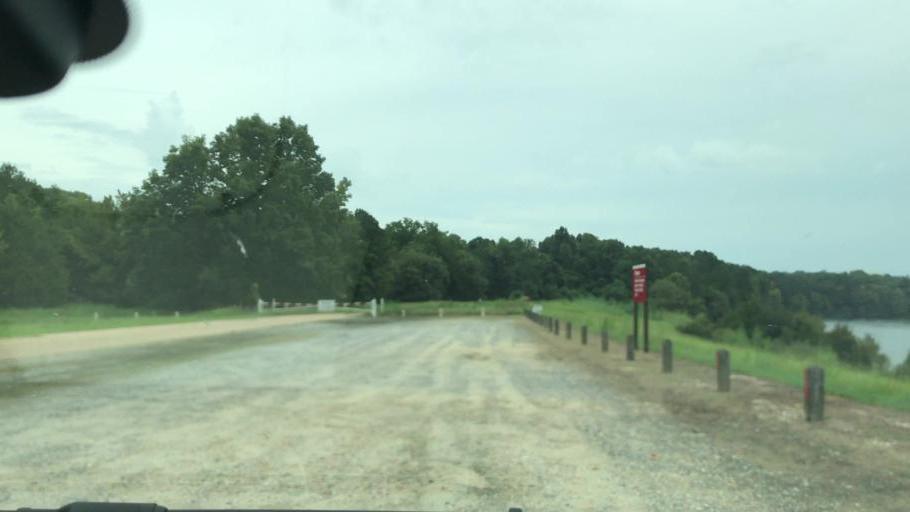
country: US
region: Georgia
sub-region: Clay County
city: Fort Gaines
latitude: 31.6243
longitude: -85.0592
